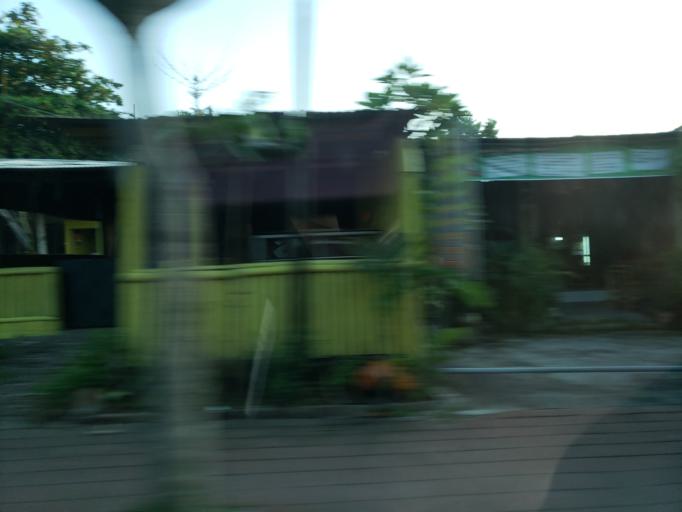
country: ID
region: Bali
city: Jimbaran
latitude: -8.8001
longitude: 115.1695
